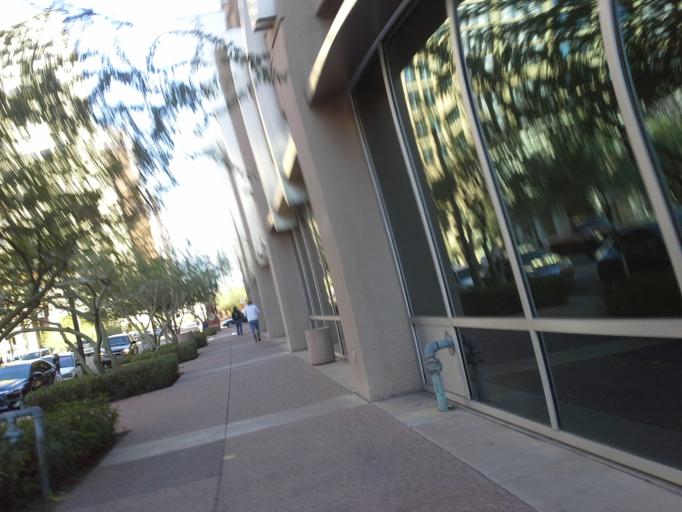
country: US
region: Arizona
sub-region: Maricopa County
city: Phoenix
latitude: 33.4482
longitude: -112.0787
